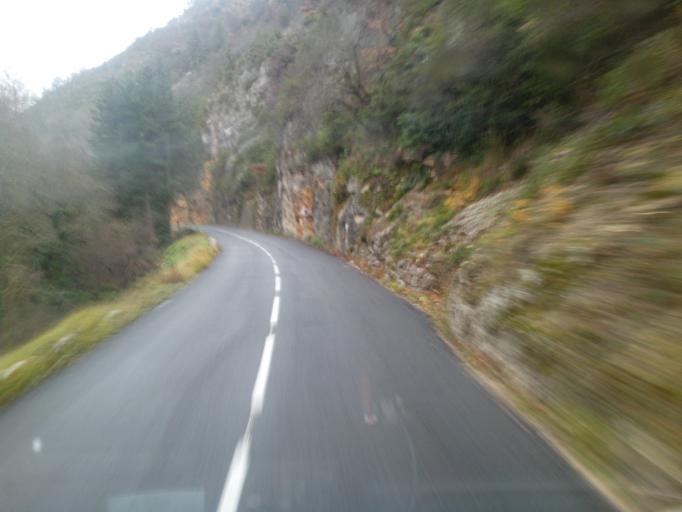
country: FR
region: Languedoc-Roussillon
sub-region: Departement de la Lozere
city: Chanac
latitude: 44.3591
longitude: 3.4055
